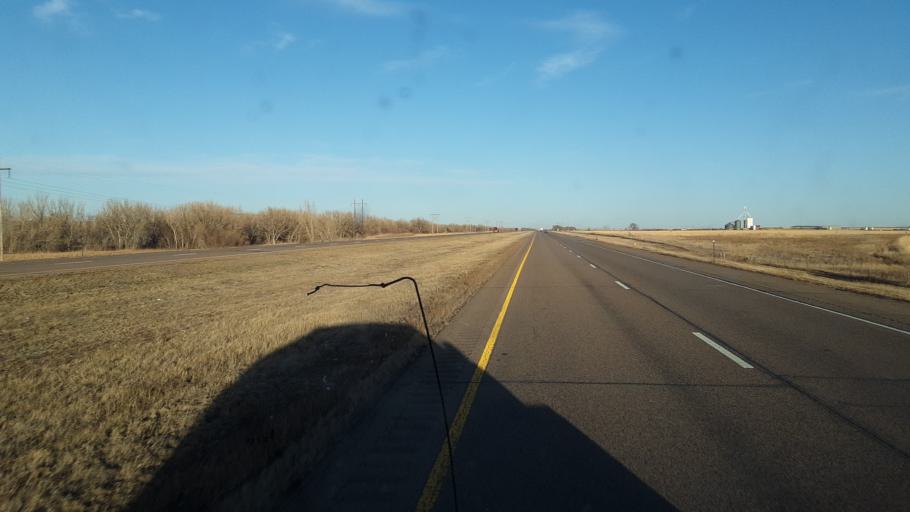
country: US
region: Nebraska
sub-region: Keith County
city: Ogallala
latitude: 41.0860
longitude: -101.8603
